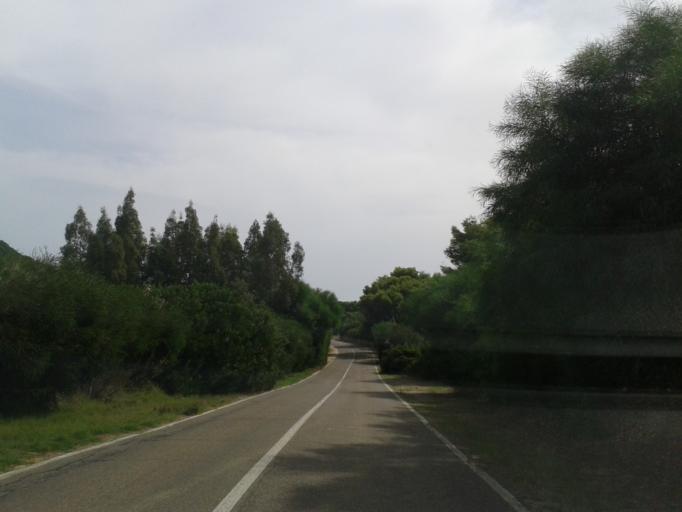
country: IT
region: Sardinia
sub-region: Provincia di Cagliari
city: Villasimius
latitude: 39.1351
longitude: 9.5038
